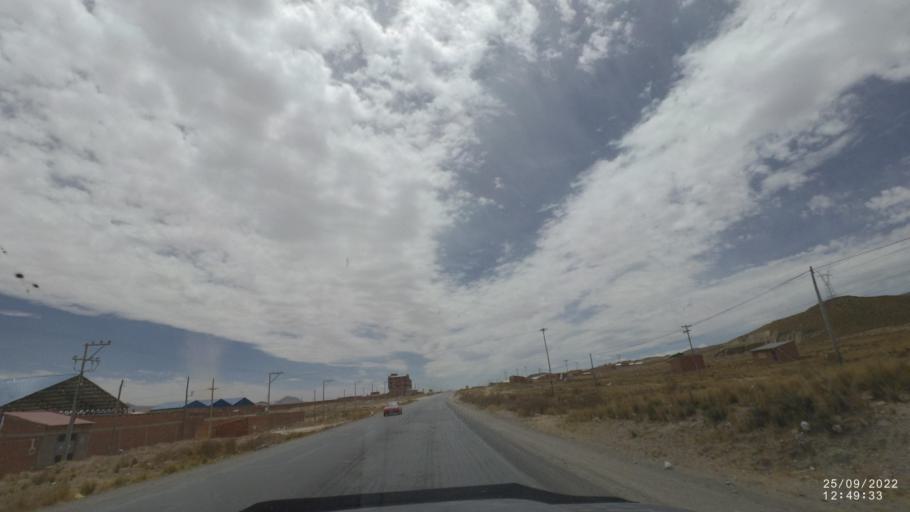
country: BO
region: Oruro
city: Oruro
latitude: -18.0092
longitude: -67.0382
